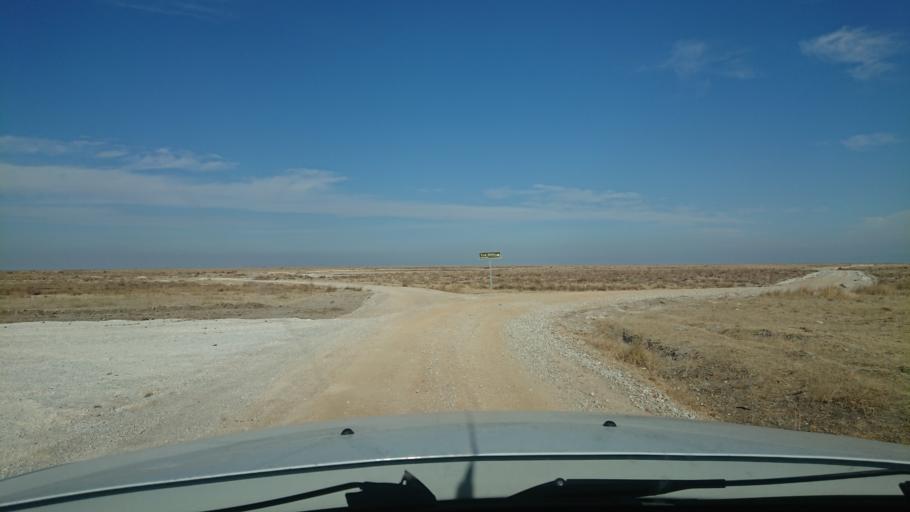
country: TR
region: Aksaray
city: Eskil
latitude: 38.4752
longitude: 33.4577
